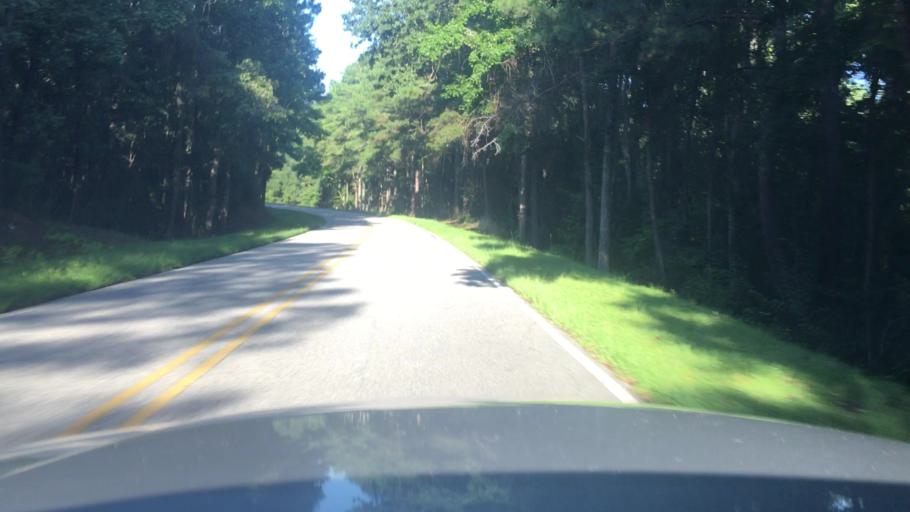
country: US
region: North Carolina
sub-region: Harnett County
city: Walkertown
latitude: 35.2269
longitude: -78.8863
